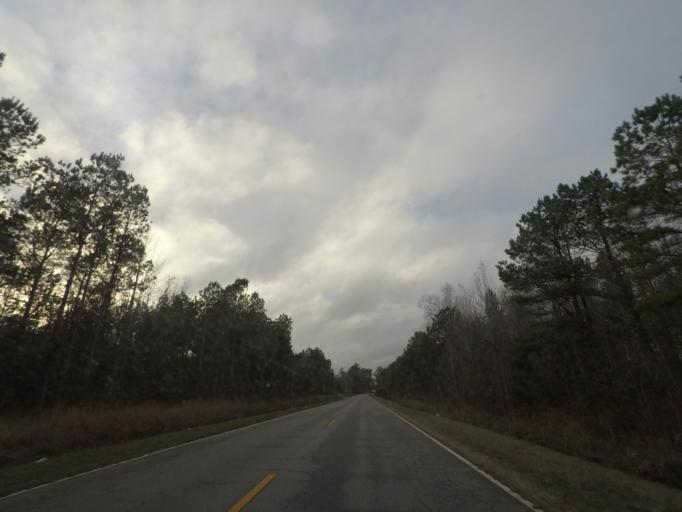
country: US
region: South Carolina
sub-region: Dorchester County
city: Saint George
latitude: 33.0497
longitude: -80.6065
